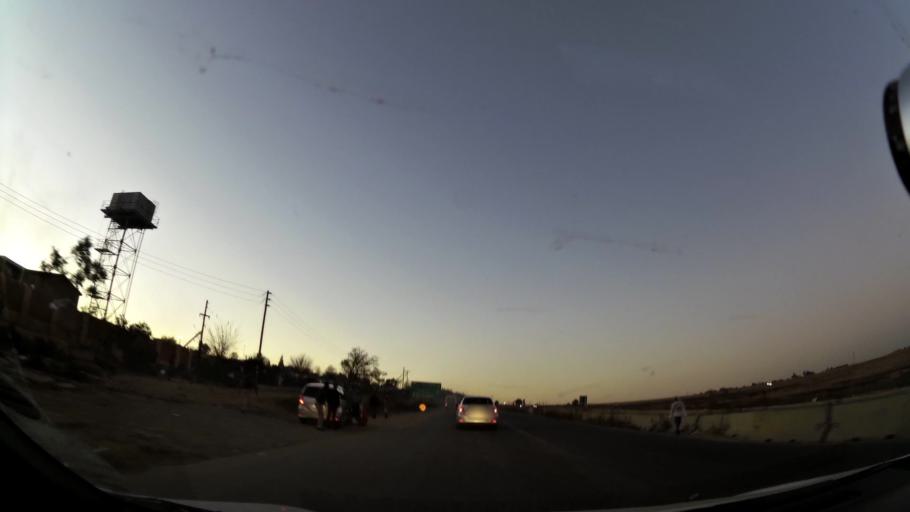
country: ZA
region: Gauteng
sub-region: City of Johannesburg Metropolitan Municipality
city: Diepsloot
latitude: -25.9223
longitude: 28.0232
